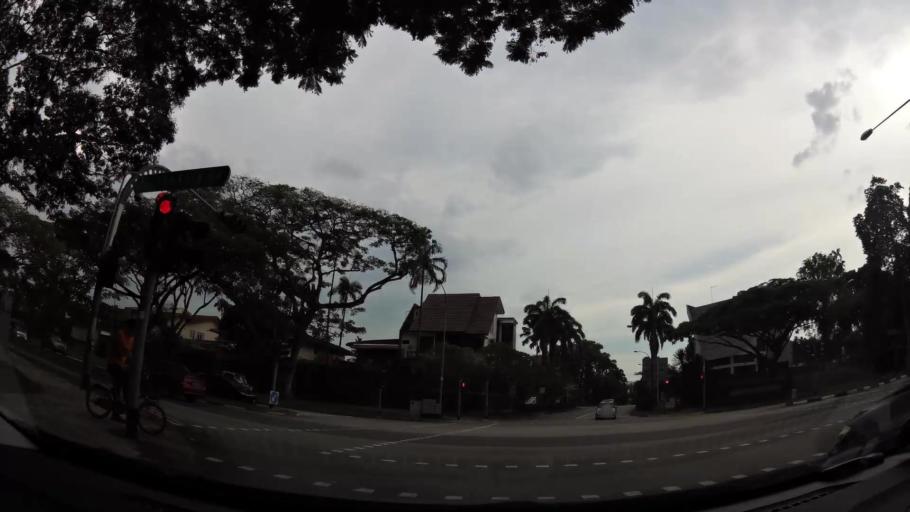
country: SG
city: Singapore
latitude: 1.3802
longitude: 103.8315
